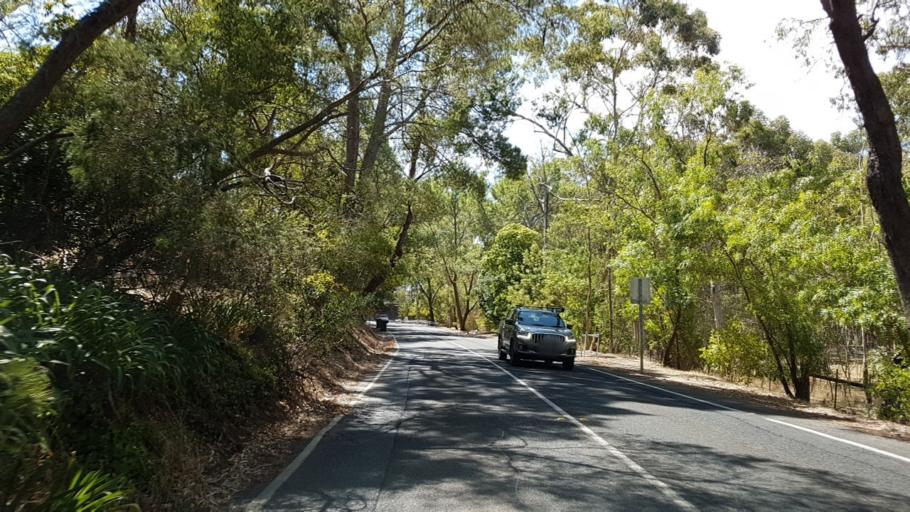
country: AU
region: South Australia
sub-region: Mitcham
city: Belair
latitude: -35.0004
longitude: 138.6326
